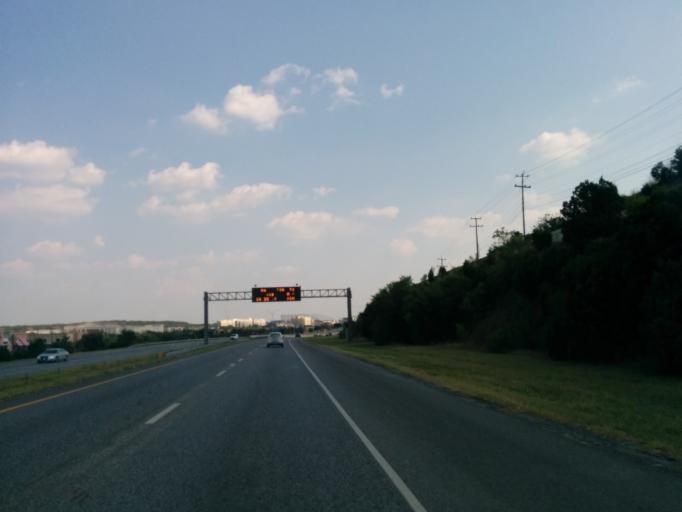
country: US
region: Texas
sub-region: Bexar County
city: Shavano Park
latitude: 29.6135
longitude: -98.6053
